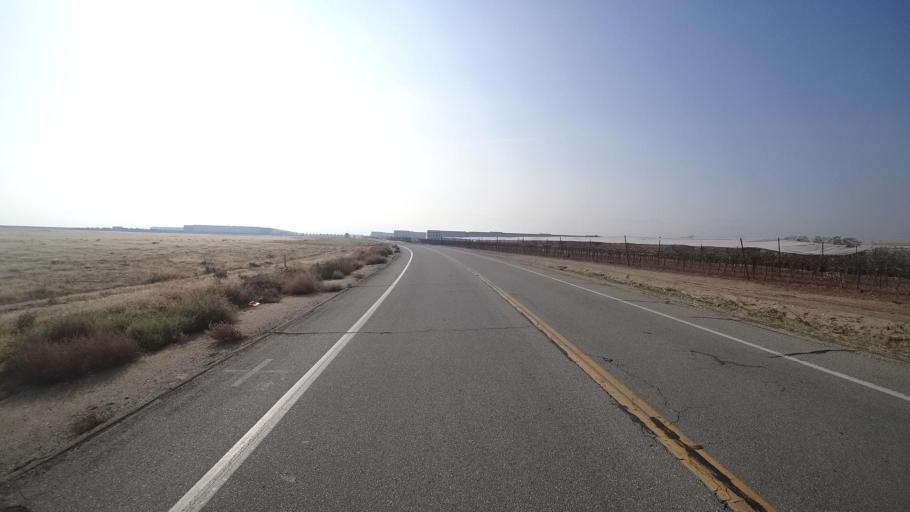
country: US
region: California
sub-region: Kern County
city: Lebec
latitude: 35.0044
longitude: -118.9434
